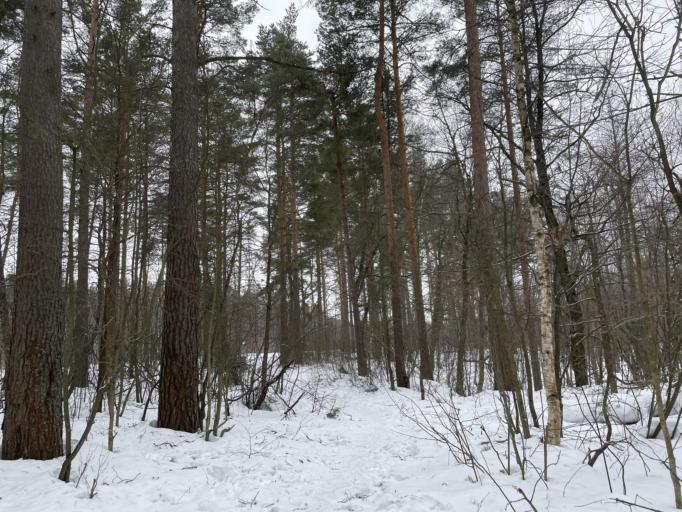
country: RU
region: Vladimir
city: Pokrov
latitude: 55.9440
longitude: 39.2410
